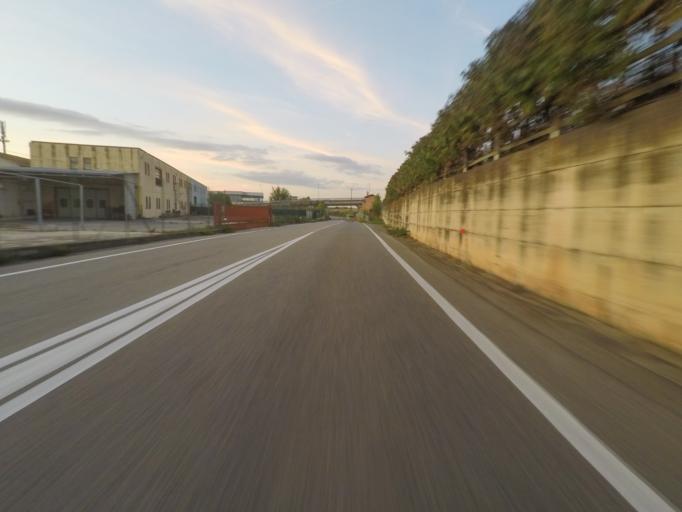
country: IT
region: Tuscany
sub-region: Provincia di Siena
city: Sinalunga
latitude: 43.2117
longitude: 11.7620
